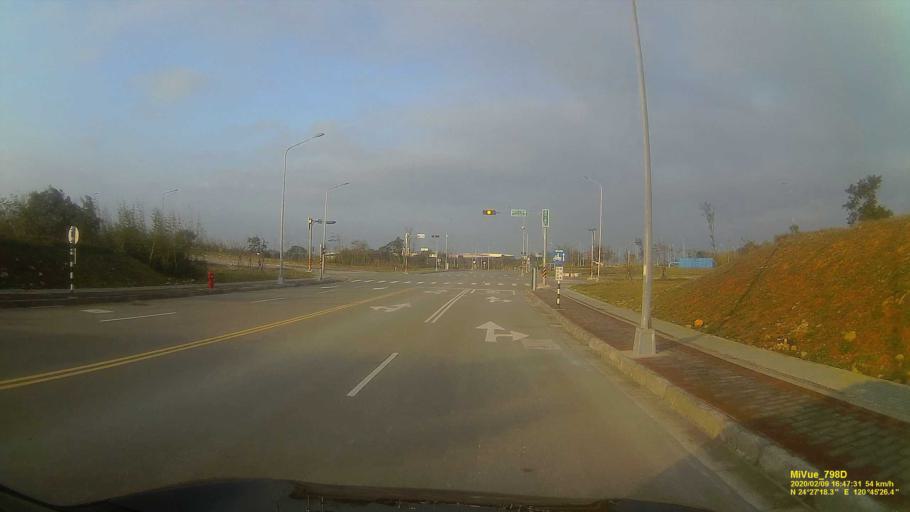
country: TW
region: Taiwan
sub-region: Miaoli
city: Miaoli
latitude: 24.4553
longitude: 120.7574
